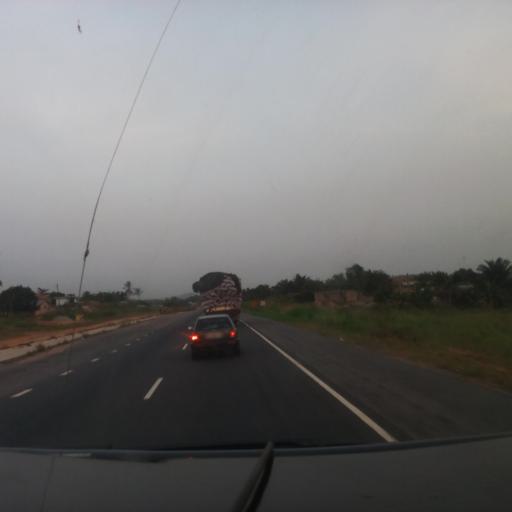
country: GH
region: Eastern
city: Nsawam
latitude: 5.8971
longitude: -0.3870
